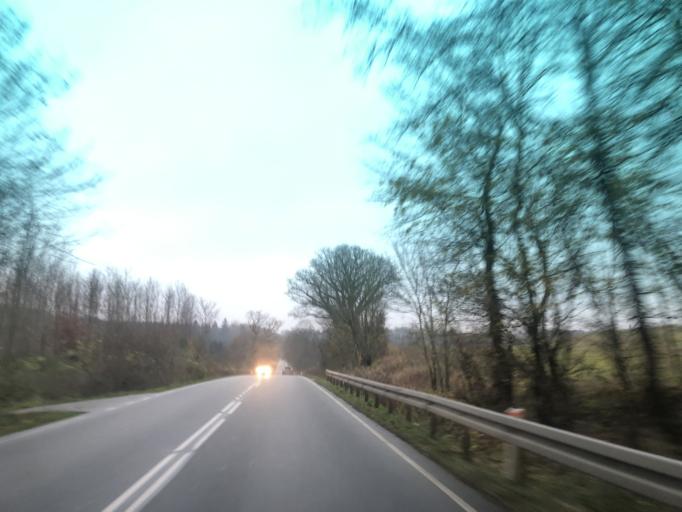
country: DK
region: South Denmark
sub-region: Nyborg Kommune
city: Ullerslev
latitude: 55.2381
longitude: 10.6509
